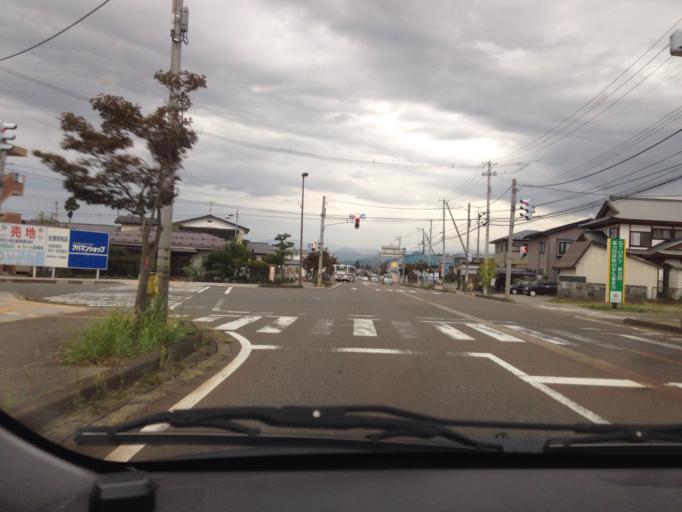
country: JP
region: Fukushima
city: Kitakata
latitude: 37.6002
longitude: 139.8908
